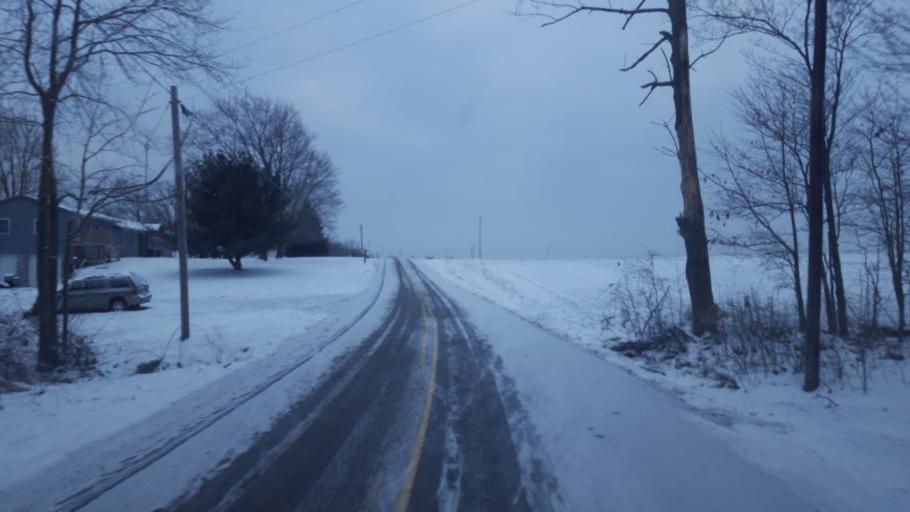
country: US
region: Pennsylvania
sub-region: Venango County
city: Sugarcreek
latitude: 41.4066
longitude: -79.9989
